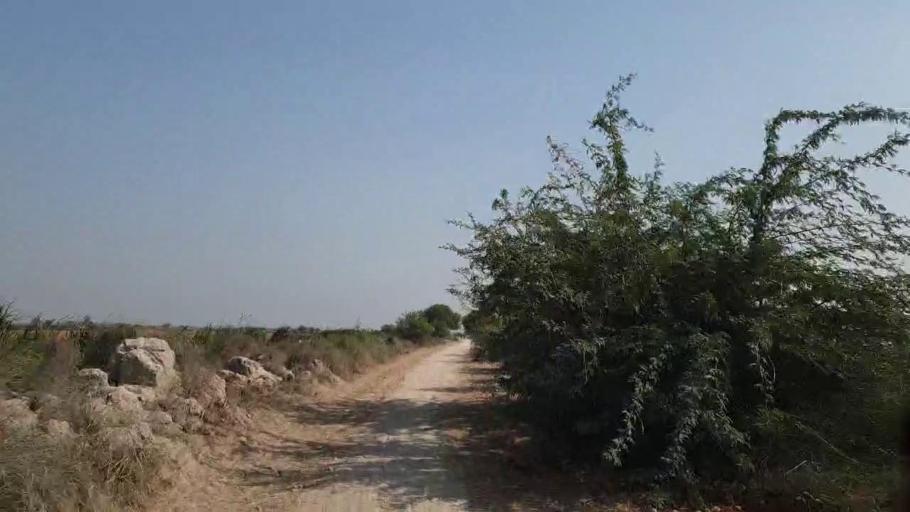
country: PK
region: Sindh
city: Tando Muhammad Khan
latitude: 25.0836
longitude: 68.4282
